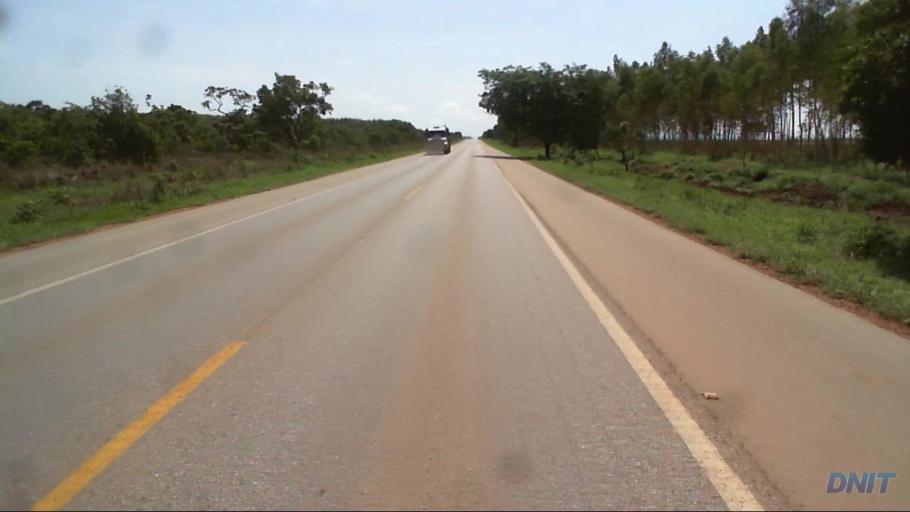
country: BR
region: Goias
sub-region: Barro Alto
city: Barro Alto
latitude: -15.2053
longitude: -48.7283
